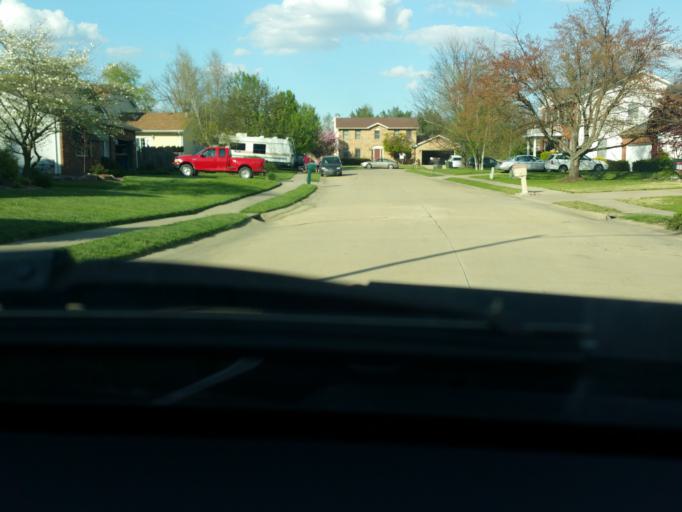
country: US
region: Illinois
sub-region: Madison County
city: Edwardsville
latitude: 38.7910
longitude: -89.9622
